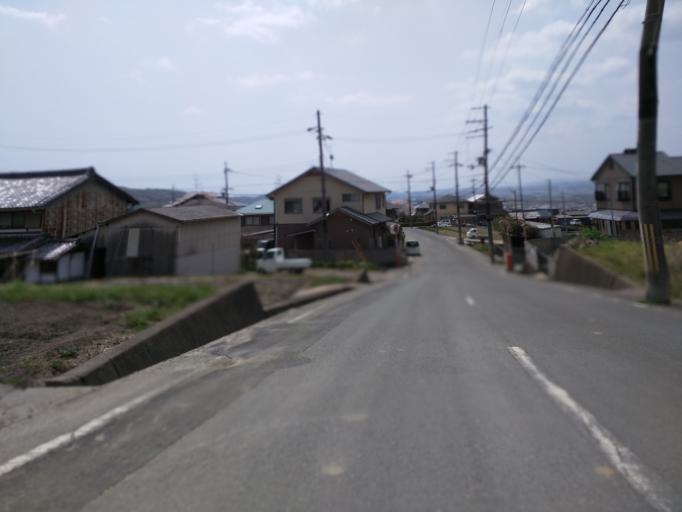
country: JP
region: Kyoto
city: Tanabe
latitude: 34.8051
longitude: 135.8141
